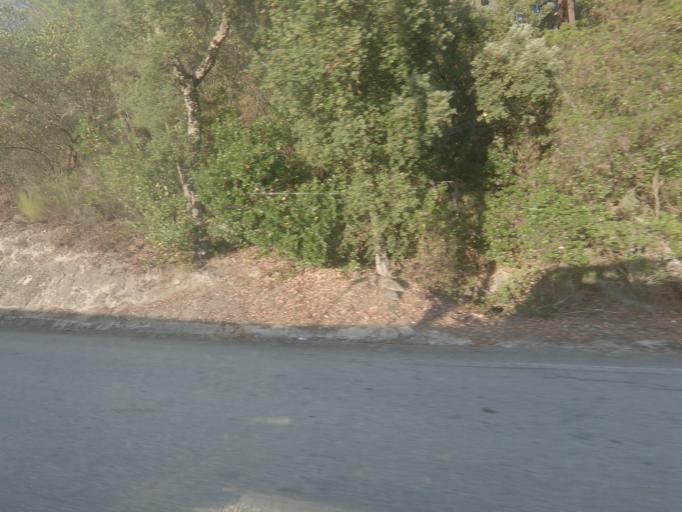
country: PT
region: Viseu
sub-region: Armamar
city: Armamar
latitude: 41.1113
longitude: -7.6758
